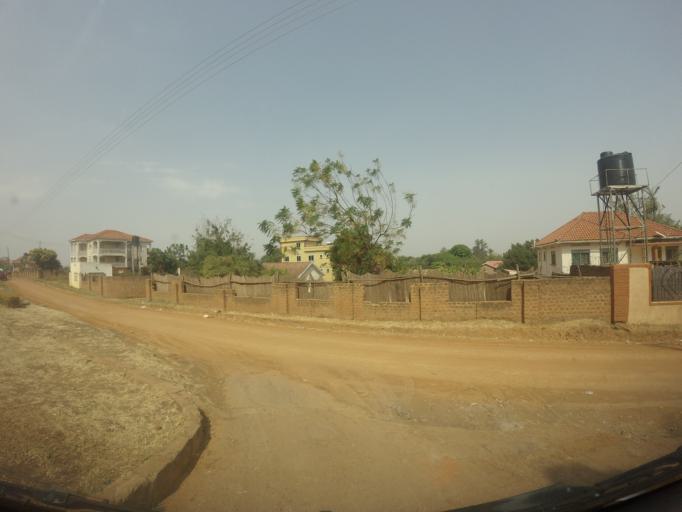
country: UG
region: Northern Region
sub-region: Arua District
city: Arua
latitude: 3.0124
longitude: 30.9171
